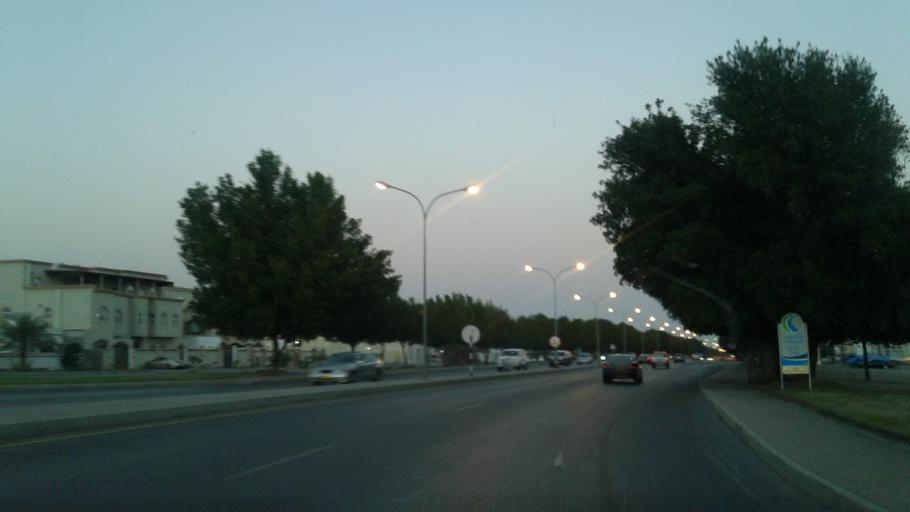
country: OM
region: Muhafazat Masqat
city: As Sib al Jadidah
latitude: 23.6141
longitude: 58.2199
